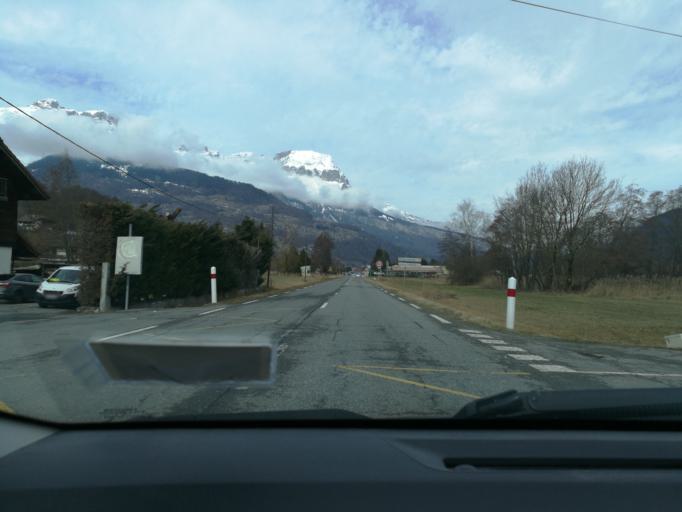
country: FR
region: Rhone-Alpes
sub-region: Departement de la Haute-Savoie
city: Domancy
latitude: 45.9197
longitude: 6.6458
